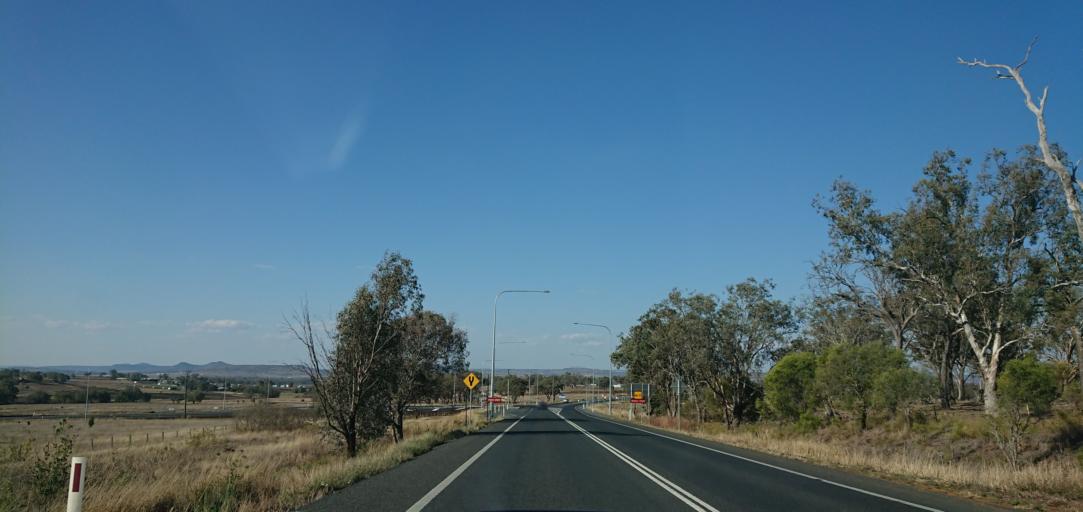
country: AU
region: Queensland
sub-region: Toowoomba
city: Westbrook
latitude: -27.6217
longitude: 151.7652
